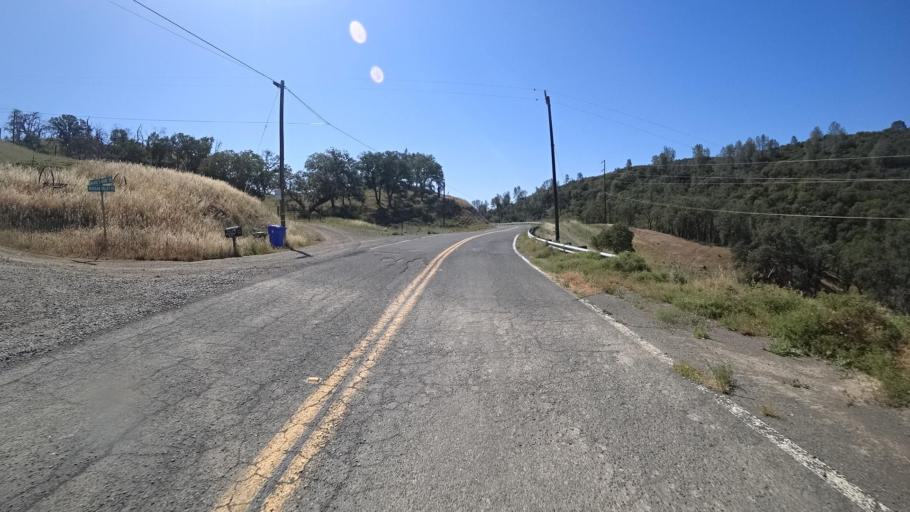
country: US
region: California
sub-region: Lake County
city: Lower Lake
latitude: 38.8926
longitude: -122.5445
